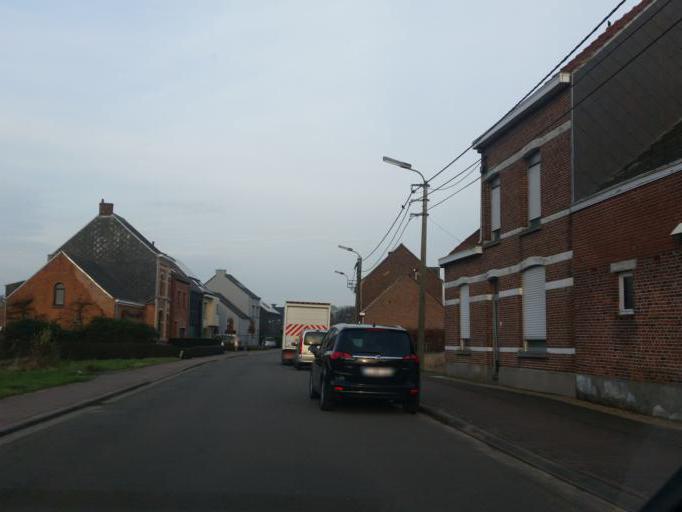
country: BE
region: Flanders
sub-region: Provincie Antwerpen
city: Duffel
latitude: 51.0647
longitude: 4.4930
